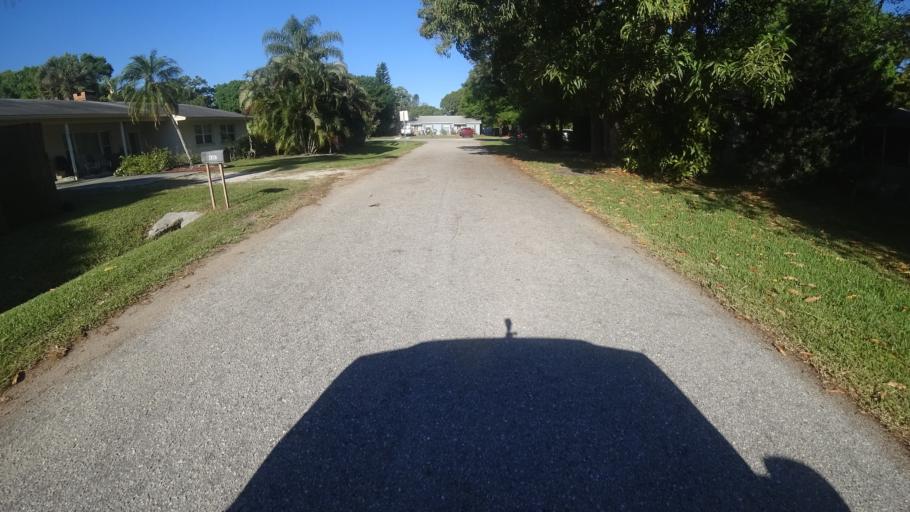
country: US
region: Florida
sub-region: Manatee County
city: West Bradenton
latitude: 27.4636
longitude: -82.6376
